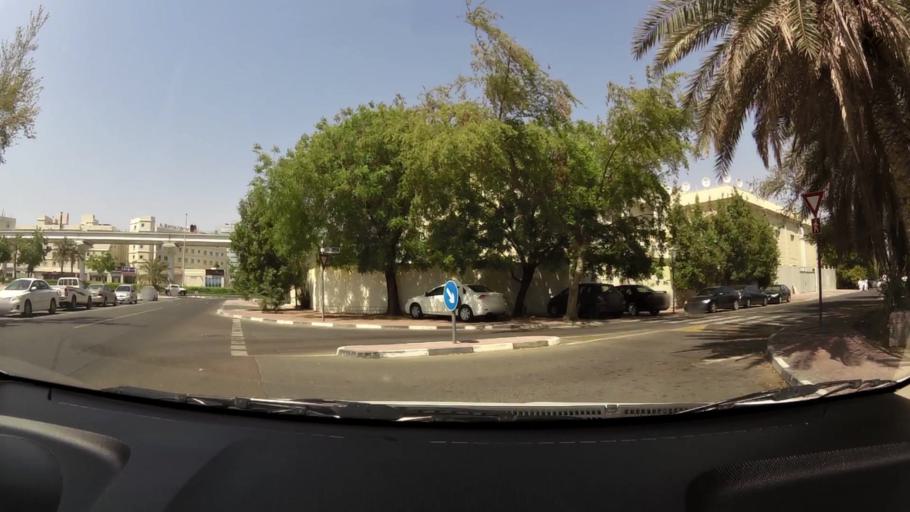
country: AE
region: Ash Shariqah
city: Sharjah
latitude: 25.2731
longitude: 55.3674
